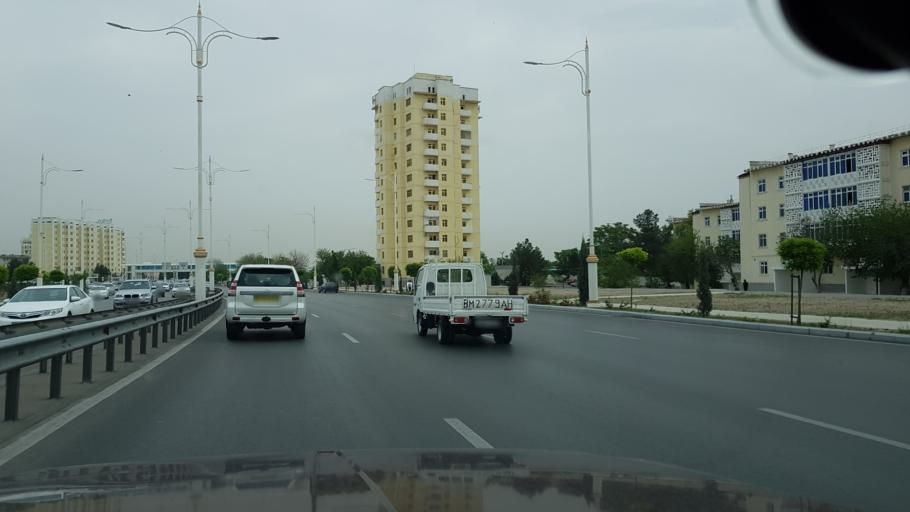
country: TM
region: Ahal
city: Ashgabat
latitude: 37.9168
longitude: 58.3896
